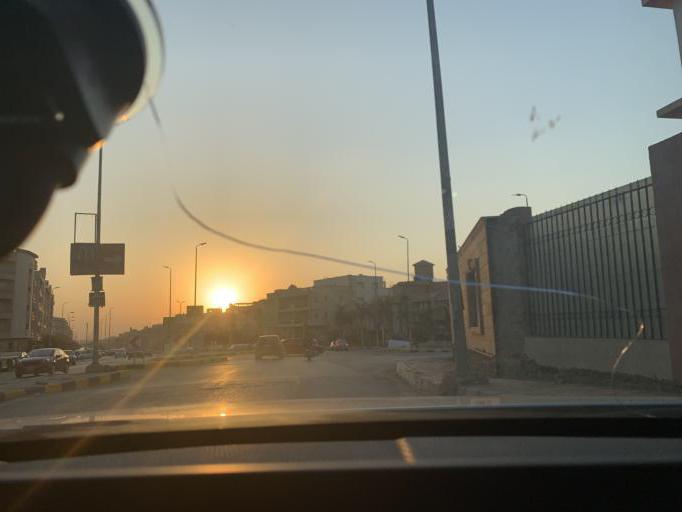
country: EG
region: Muhafazat al Qahirah
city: Cairo
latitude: 30.0057
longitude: 31.4555
